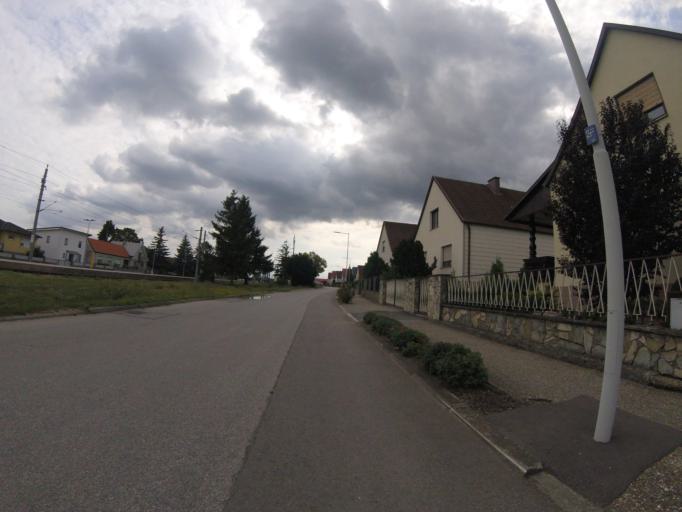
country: AT
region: Burgenland
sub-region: Eisenstadt-Umgebung
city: Breitenbrunn
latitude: 47.9073
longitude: 16.6994
